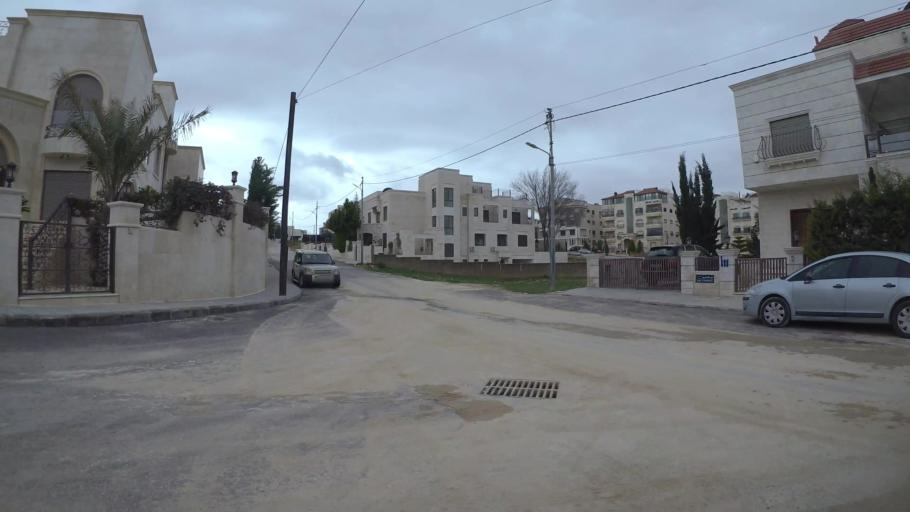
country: JO
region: Amman
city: Wadi as Sir
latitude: 31.9612
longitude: 35.8231
